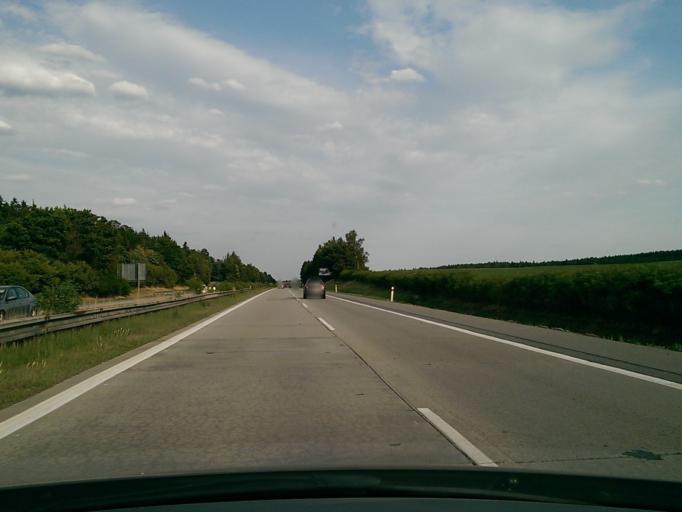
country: CZ
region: Vysocina
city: Dobronin
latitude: 49.4394
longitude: 15.6376
